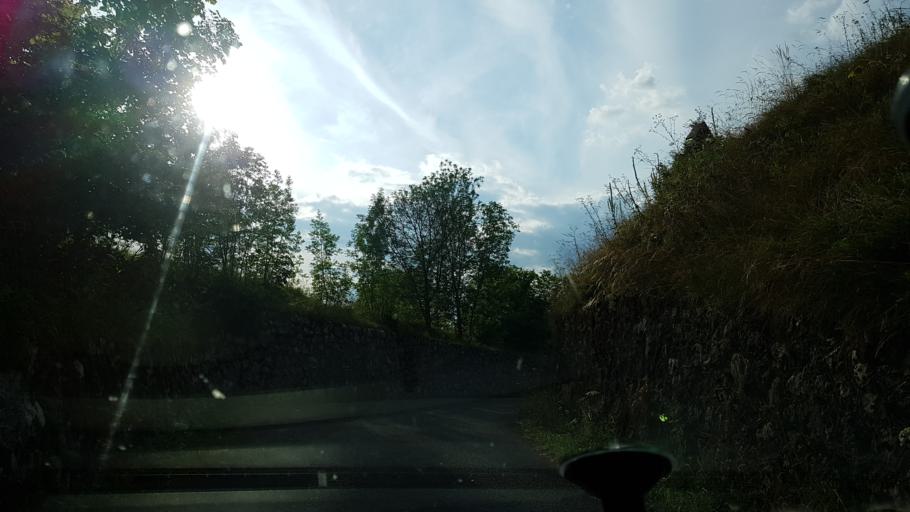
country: IT
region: Friuli Venezia Giulia
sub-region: Provincia di Udine
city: Prato
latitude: 46.3592
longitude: 13.3557
